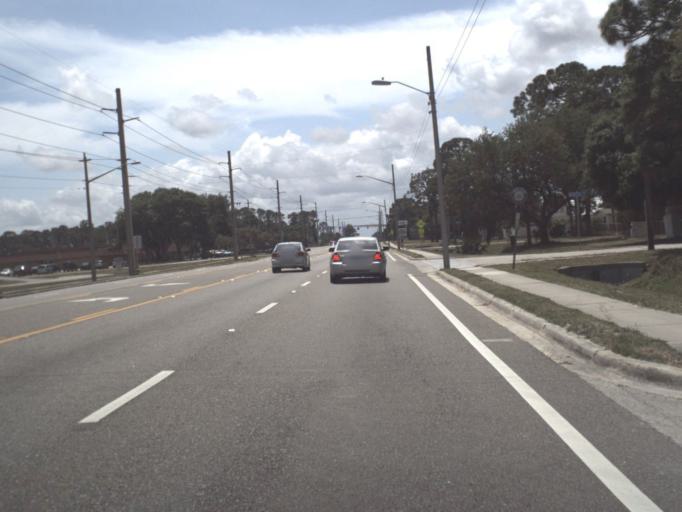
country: US
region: Florida
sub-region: Brevard County
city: Rockledge
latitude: 28.3275
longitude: -80.7428
